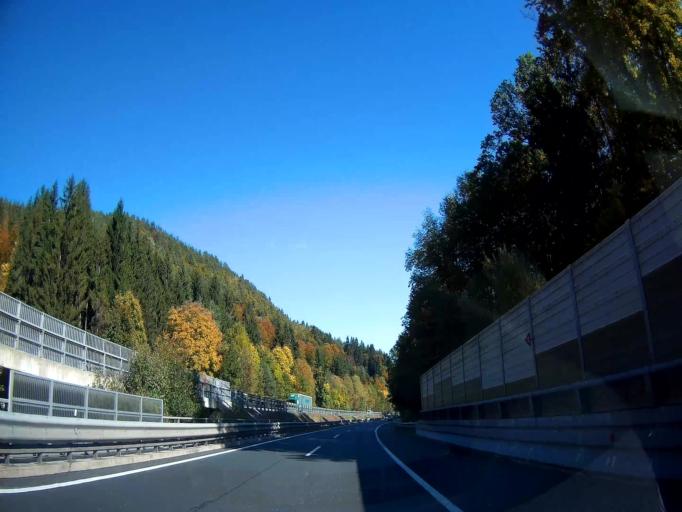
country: AT
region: Carinthia
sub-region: Politischer Bezirk Villach Land
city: Velden am Woerthersee
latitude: 46.6245
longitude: 14.0543
